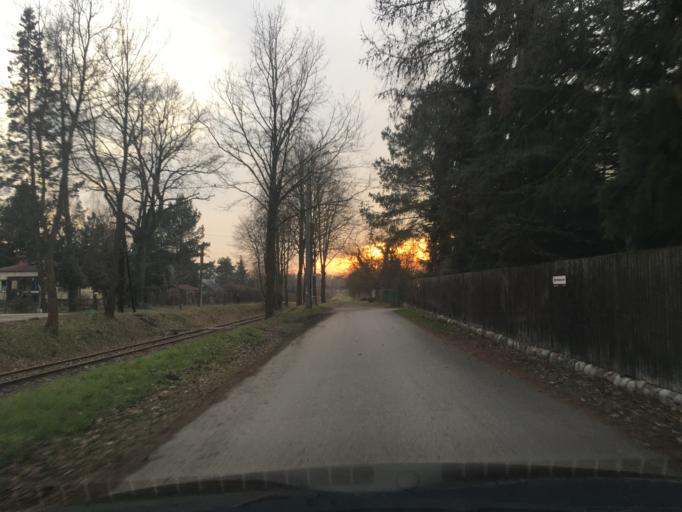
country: PL
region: Masovian Voivodeship
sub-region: Powiat piaseczynski
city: Lesznowola
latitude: 52.0344
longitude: 20.9585
